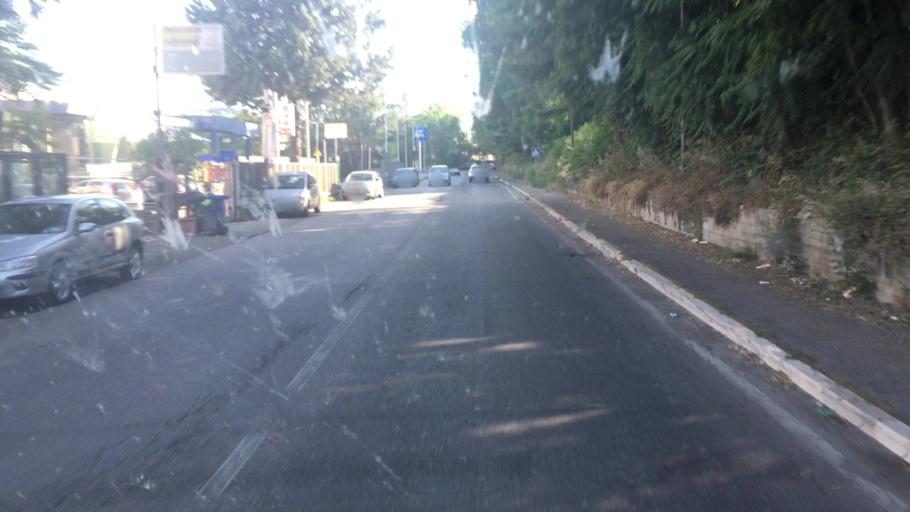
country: IT
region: Basilicate
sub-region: Provincia di Potenza
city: Potenza
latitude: 40.6323
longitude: 15.8118
